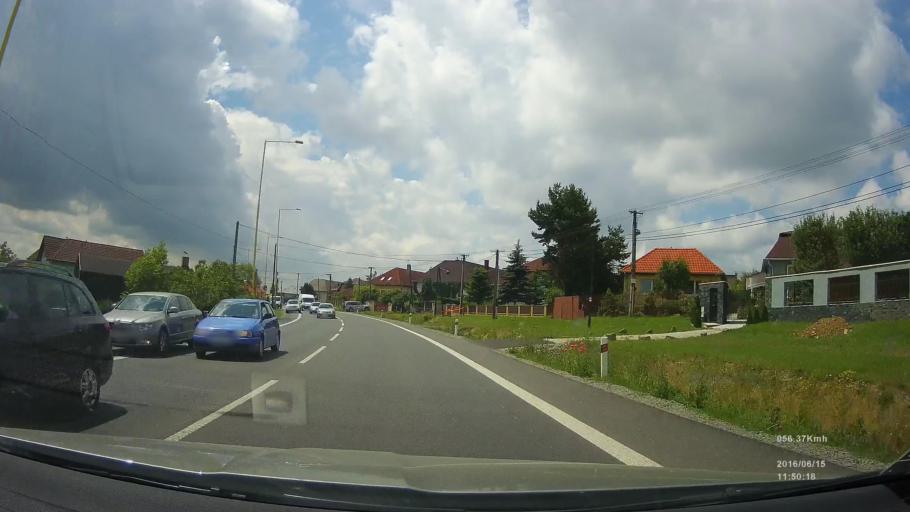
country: SK
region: Kosicky
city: Kosice
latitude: 48.7343
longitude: 21.2949
